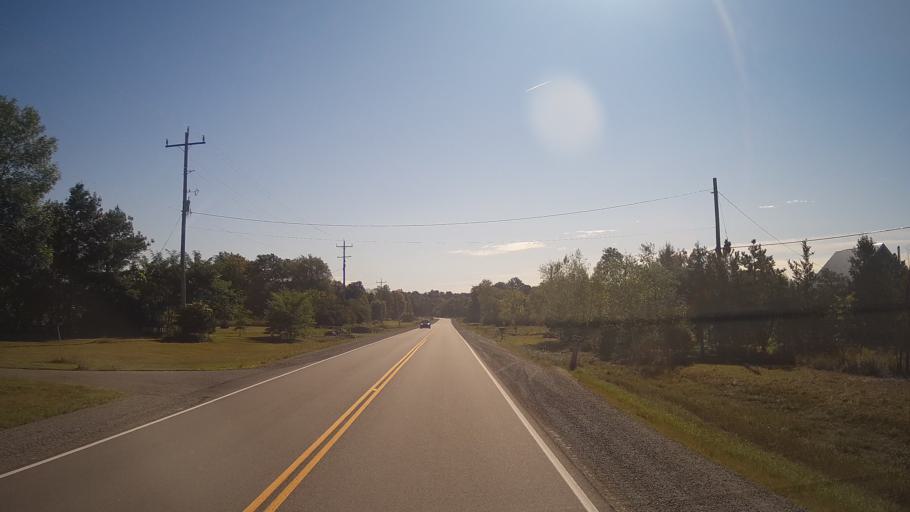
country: CA
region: Ontario
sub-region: Lanark County
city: Smiths Falls
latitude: 44.6258
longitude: -75.9986
